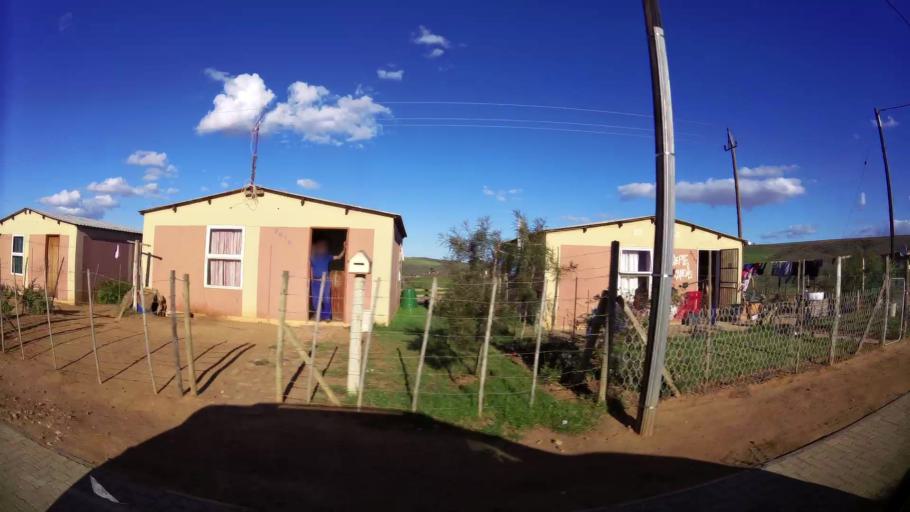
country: ZA
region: Western Cape
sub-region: Eden District Municipality
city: Riversdale
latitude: -34.1101
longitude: 20.9650
